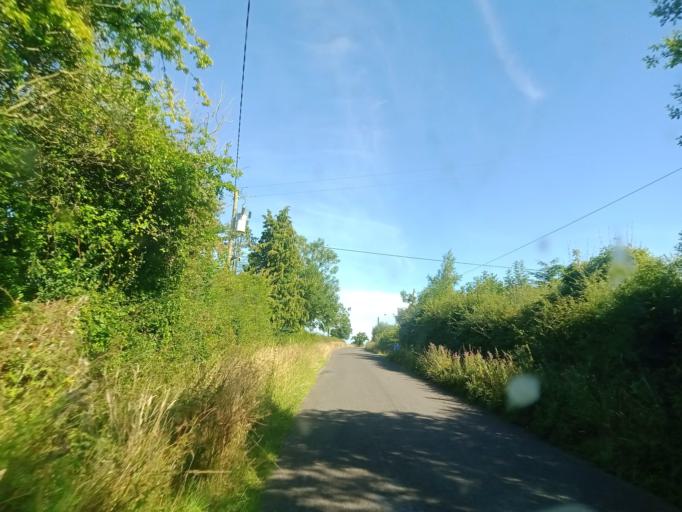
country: IE
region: Leinster
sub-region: Kilkenny
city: Ballyragget
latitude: 52.7643
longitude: -7.4085
